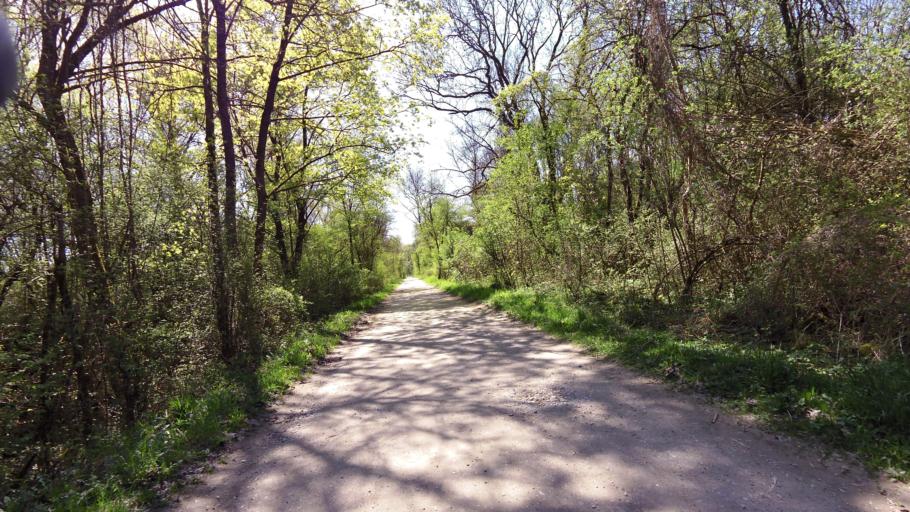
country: DE
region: Bavaria
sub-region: Lower Bavaria
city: Ergolding
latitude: 48.5623
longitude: 12.1870
